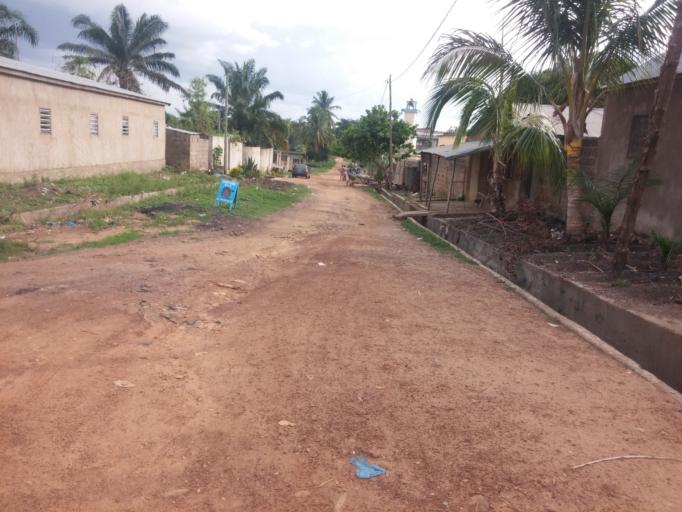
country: TG
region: Kara
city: Kara
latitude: 9.5481
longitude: 1.2045
